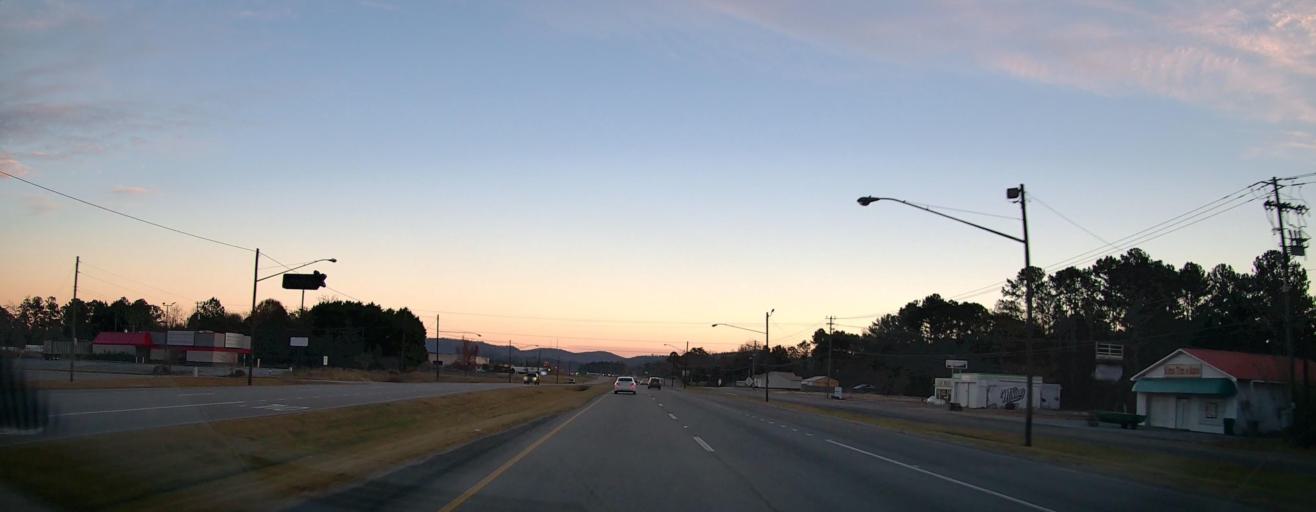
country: US
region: Alabama
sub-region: Etowah County
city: Glencoe
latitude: 33.9732
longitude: -85.9506
